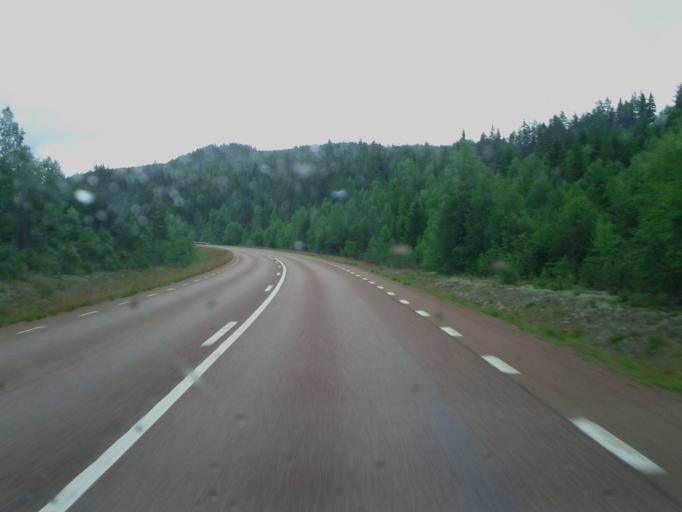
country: SE
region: Dalarna
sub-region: Alvdalens Kommun
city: AElvdalen
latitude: 61.2688
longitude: 13.8255
